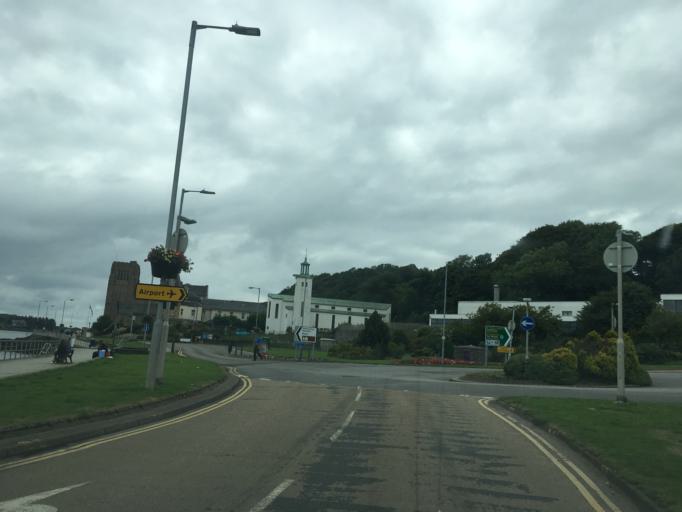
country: GB
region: Scotland
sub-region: Argyll and Bute
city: Oban
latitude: 56.4180
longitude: -5.4755
